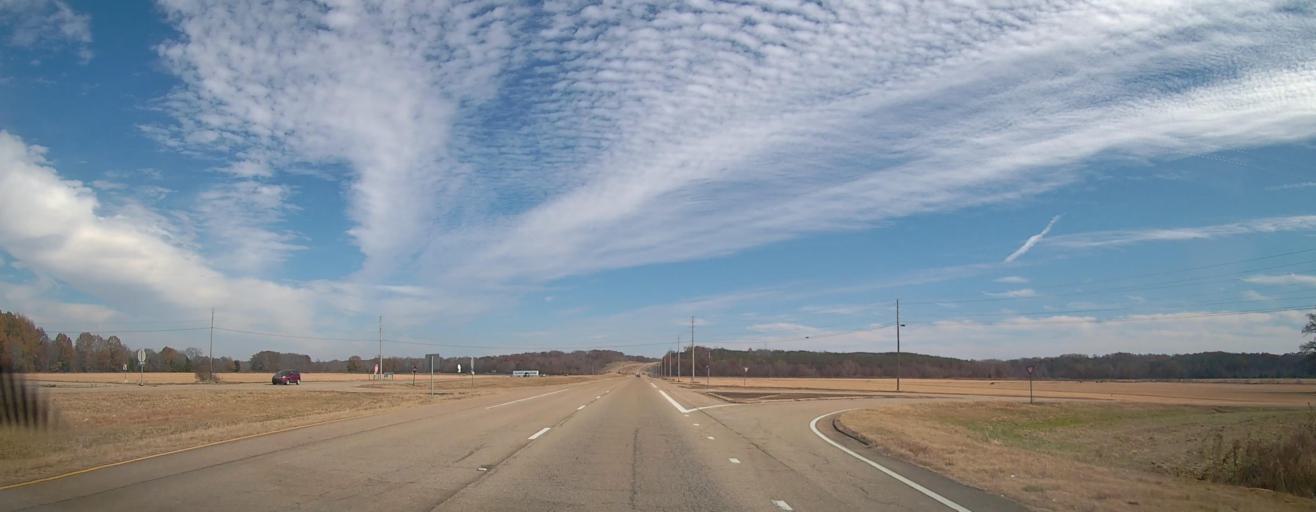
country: US
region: Mississippi
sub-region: Alcorn County
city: Corinth
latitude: 34.9315
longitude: -88.6653
